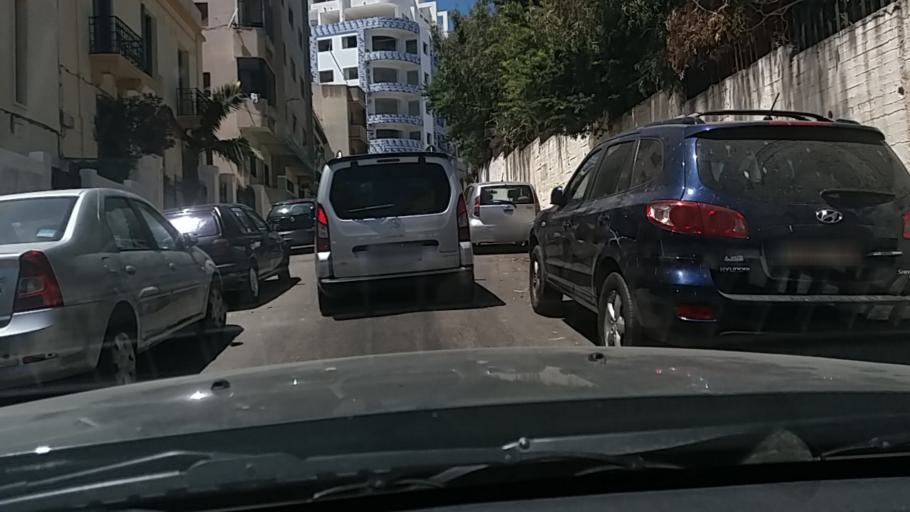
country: MA
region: Tanger-Tetouan
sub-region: Tanger-Assilah
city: Tangier
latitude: 35.7870
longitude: -5.8165
